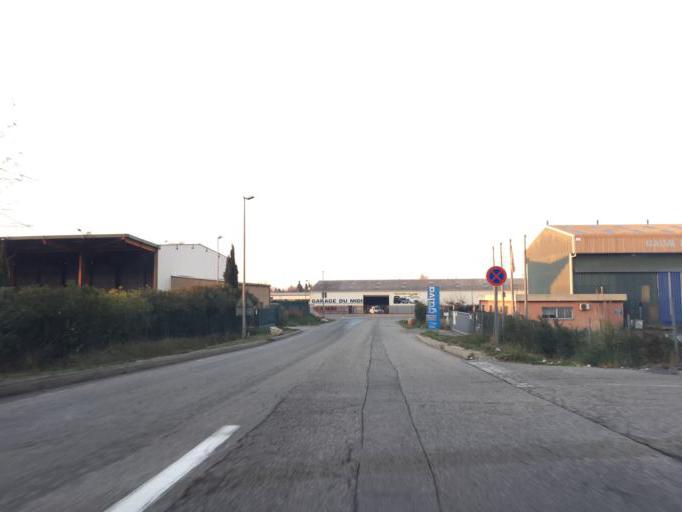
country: FR
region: Provence-Alpes-Cote d'Azur
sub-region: Departement du Vaucluse
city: Cavaillon
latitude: 43.8219
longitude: 5.0212
